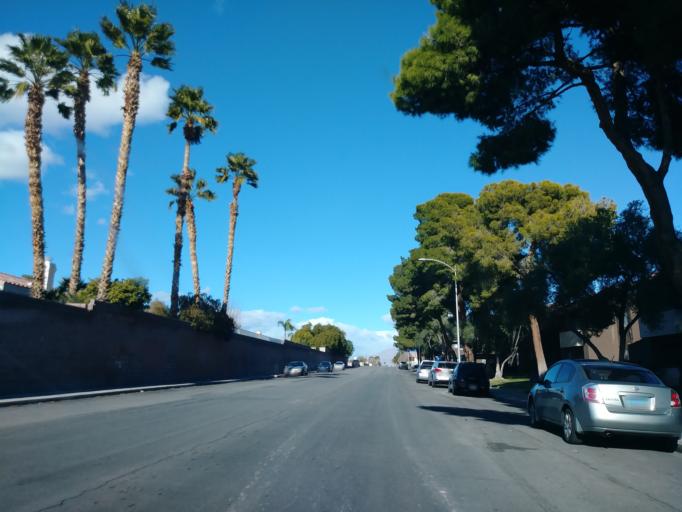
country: US
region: Nevada
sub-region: Clark County
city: Spring Valley
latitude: 36.1465
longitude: -115.2124
